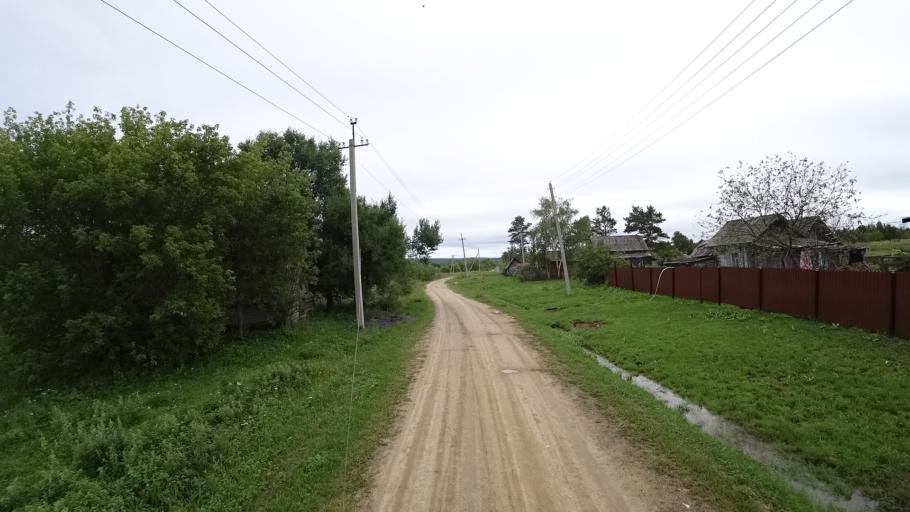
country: RU
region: Primorskiy
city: Rettikhovka
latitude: 44.1399
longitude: 132.6418
